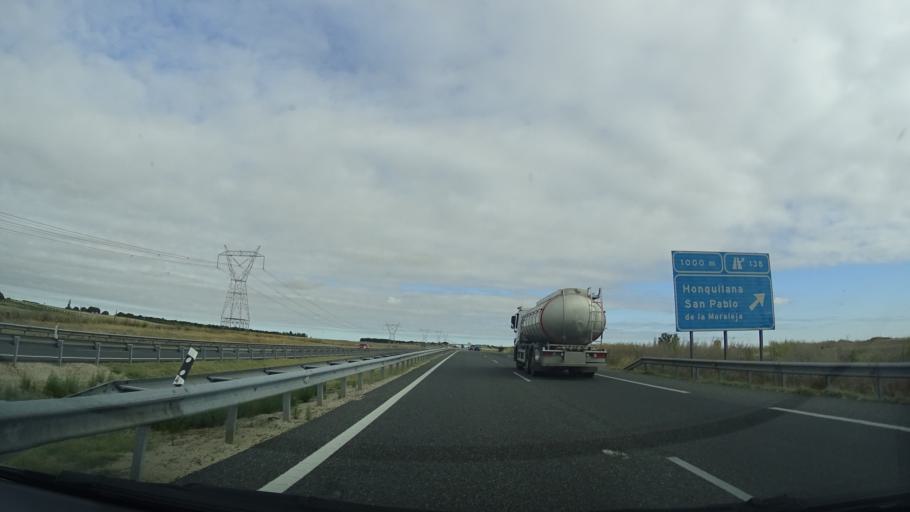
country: ES
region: Castille and Leon
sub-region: Provincia de Avila
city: Palacios de Goda
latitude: 41.1387
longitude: -4.7806
